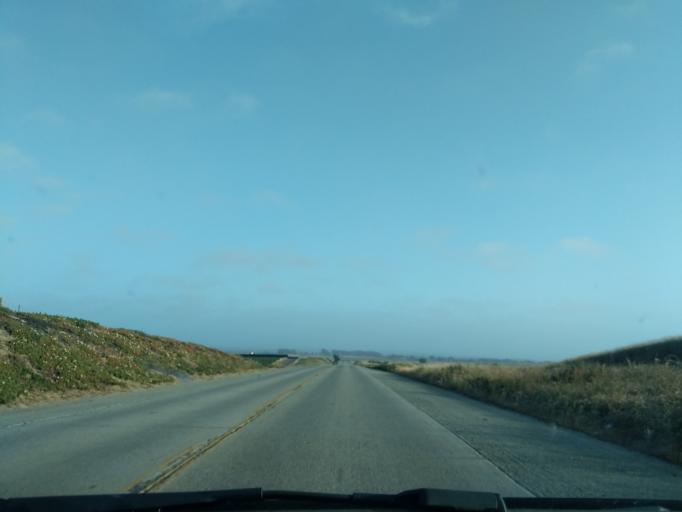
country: US
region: California
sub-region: Monterey County
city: Marina
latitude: 36.7150
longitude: -121.7881
